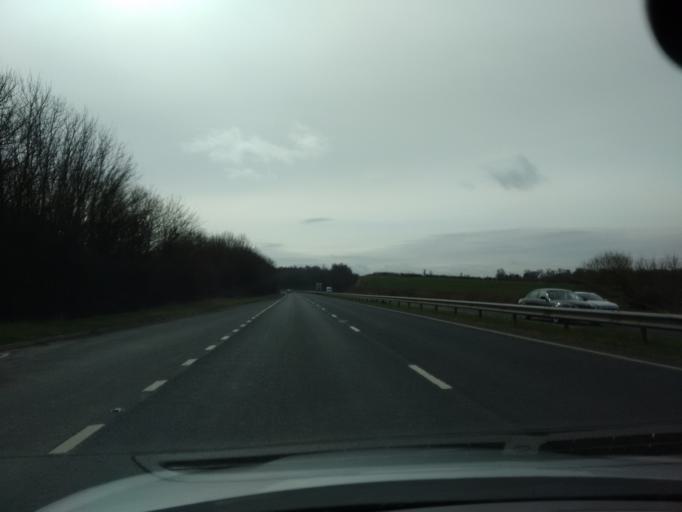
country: GB
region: England
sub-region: Warwickshire
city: Alcester
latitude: 52.2149
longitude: -1.8827
